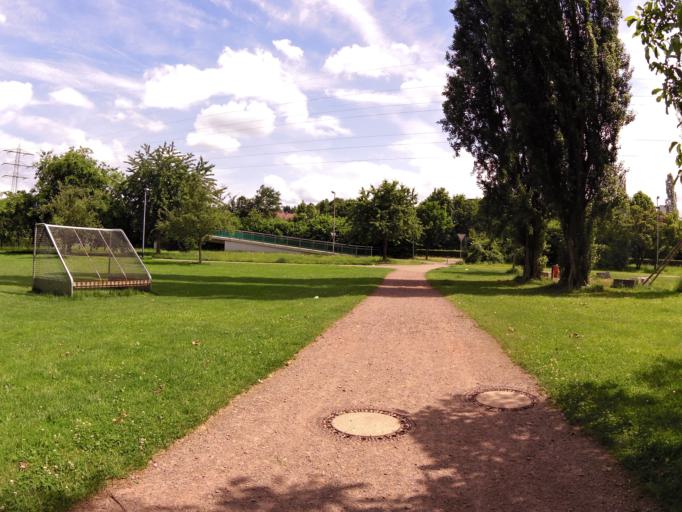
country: DE
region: Baden-Wuerttemberg
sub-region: Freiburg Region
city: Lahr
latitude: 48.3359
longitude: 7.8509
